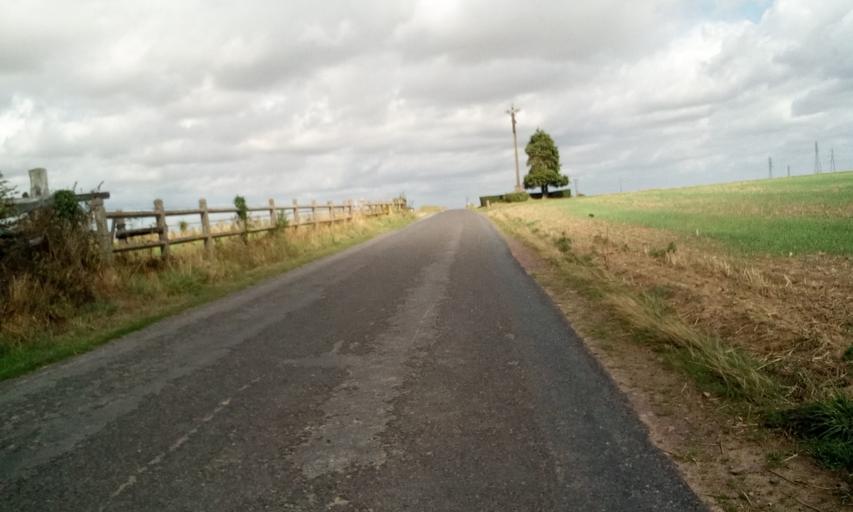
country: FR
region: Lower Normandy
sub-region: Departement du Calvados
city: Cheux
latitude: 49.1965
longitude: -0.5362
